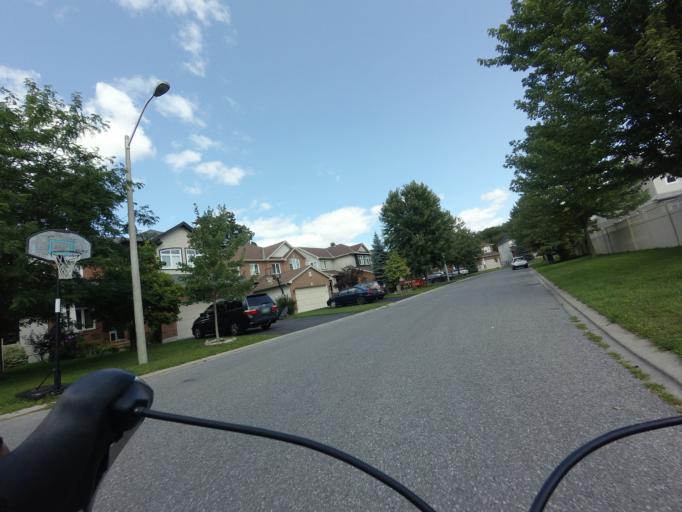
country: CA
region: Ontario
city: Bells Corners
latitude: 45.2975
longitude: -75.8516
